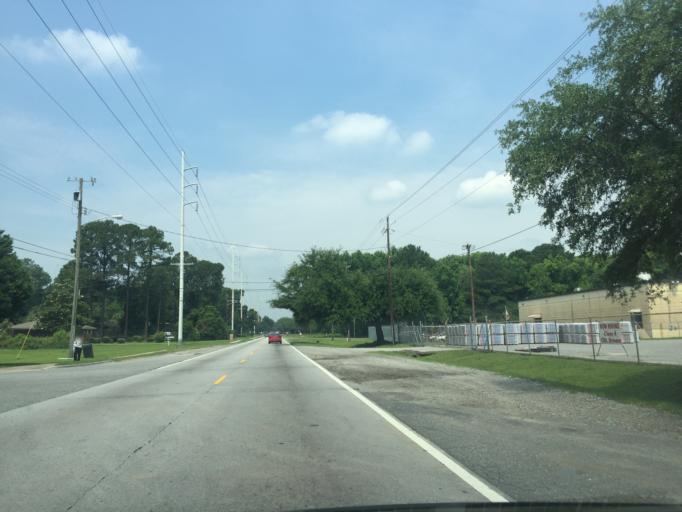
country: US
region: Georgia
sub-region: Chatham County
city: Savannah
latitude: 32.0515
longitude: -81.1299
